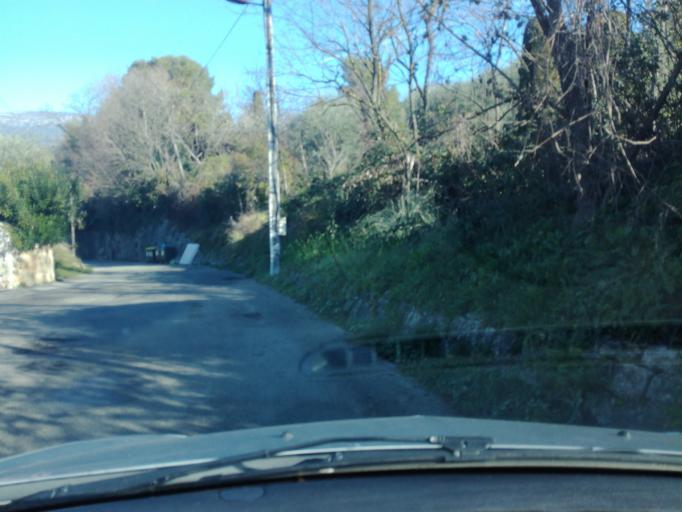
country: FR
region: Provence-Alpes-Cote d'Azur
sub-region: Departement des Alpes-Maritimes
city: Grasse
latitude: 43.6464
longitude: 6.9060
